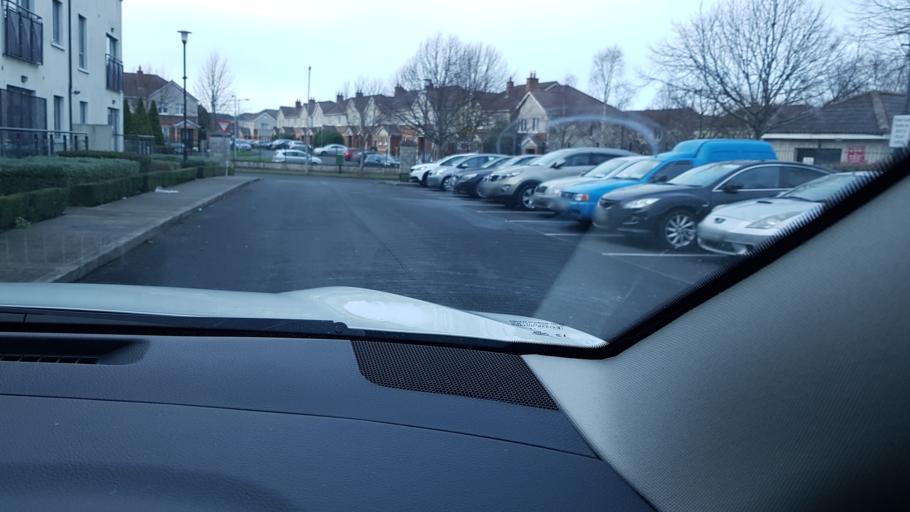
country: IE
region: Leinster
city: Hartstown
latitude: 53.3997
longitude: -6.4363
